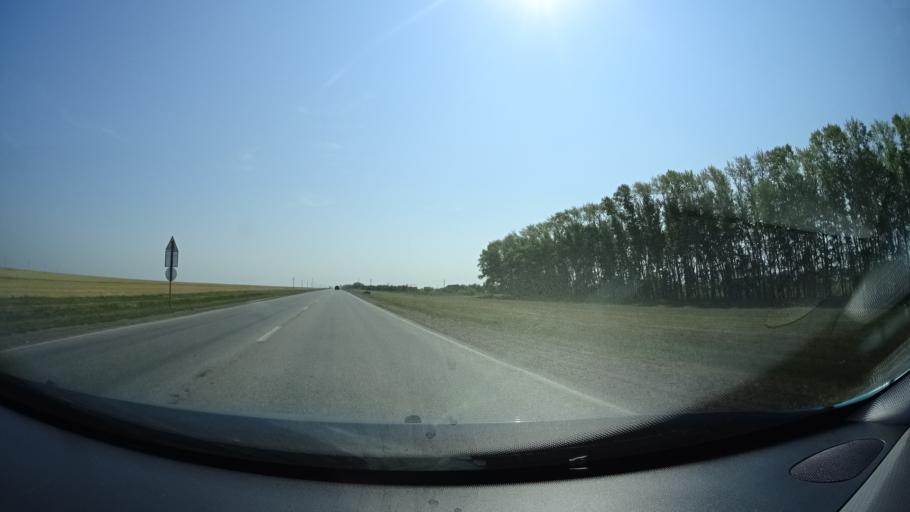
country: RU
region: Bashkortostan
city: Kabakovo
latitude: 54.4308
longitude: 56.0205
